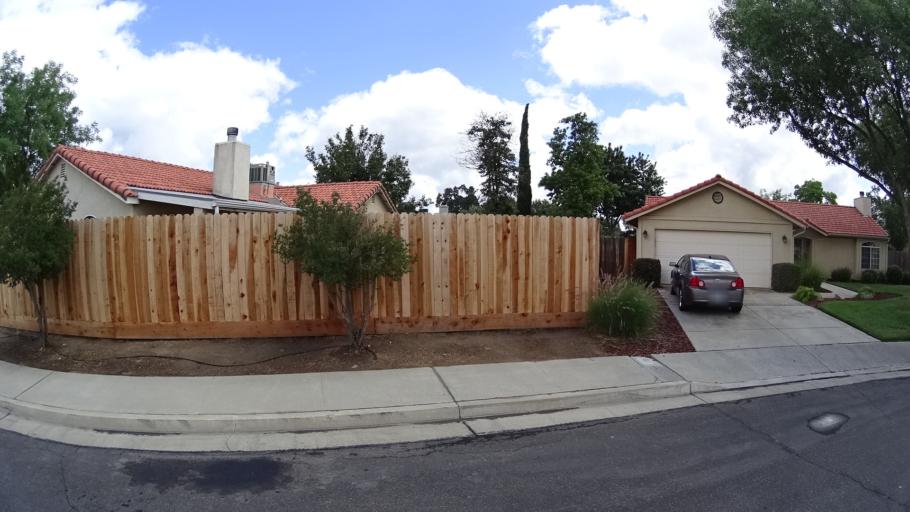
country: US
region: California
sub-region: Kings County
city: Lucerne
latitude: 36.3556
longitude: -119.6570
